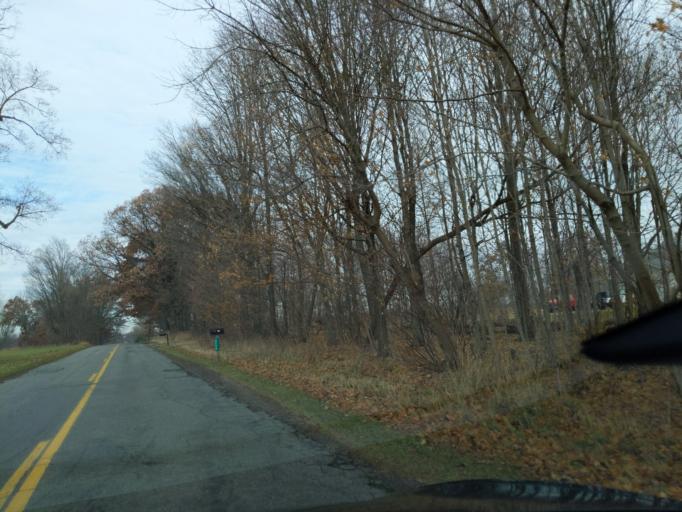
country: US
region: Michigan
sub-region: Ingham County
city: Leslie
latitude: 42.4571
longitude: -84.5019
